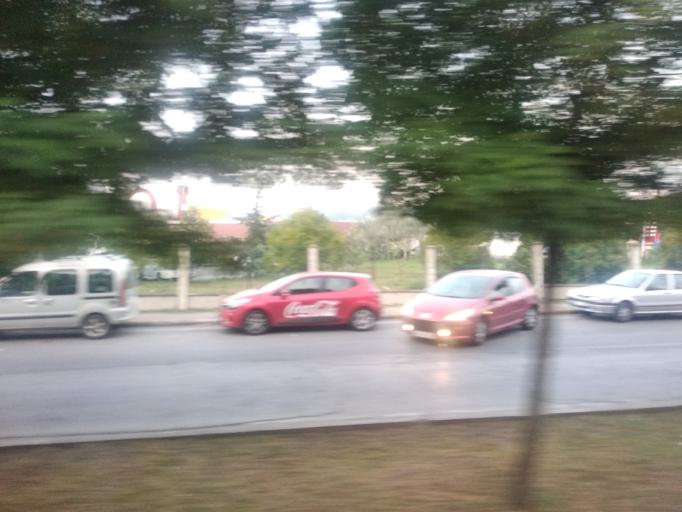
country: TR
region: Samsun
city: Samsun
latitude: 41.2863
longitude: 36.2882
